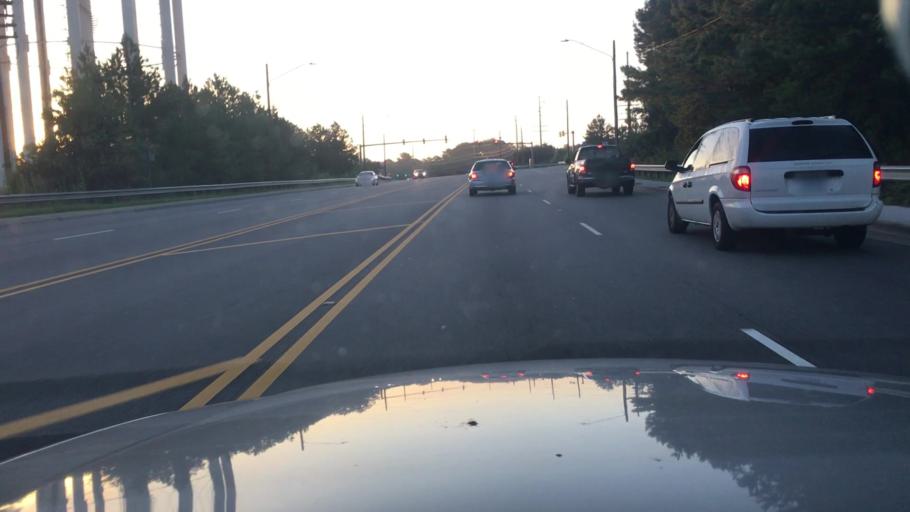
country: US
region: North Carolina
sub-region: Cumberland County
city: Fayetteville
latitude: 35.0595
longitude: -78.9565
